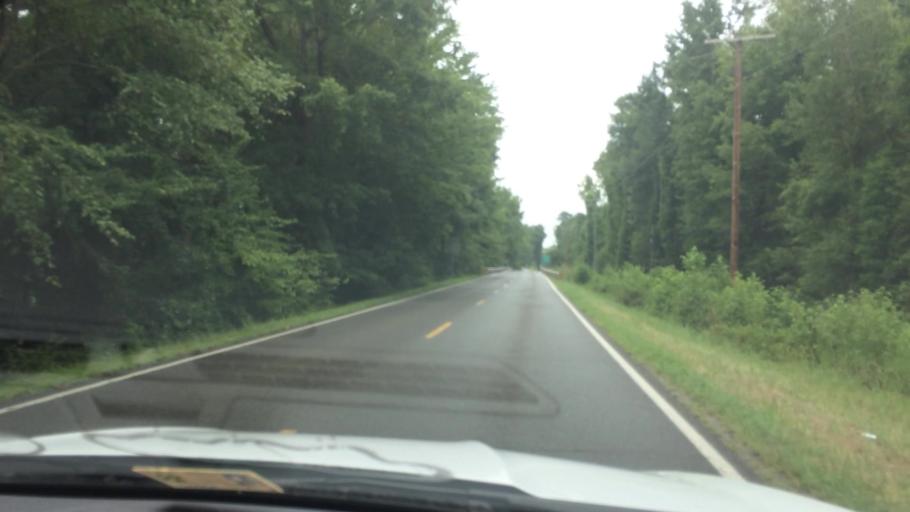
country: US
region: Virginia
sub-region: Charles City County
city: Charles City
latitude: 37.4274
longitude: -77.0388
